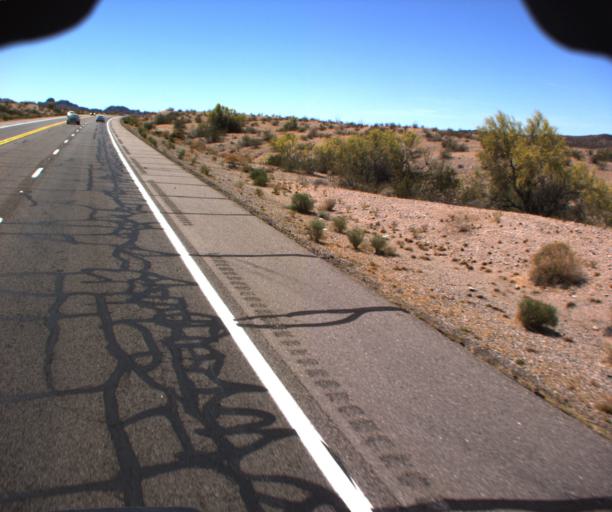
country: US
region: Arizona
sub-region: Mohave County
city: Desert Hills
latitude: 34.6926
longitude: -114.3019
